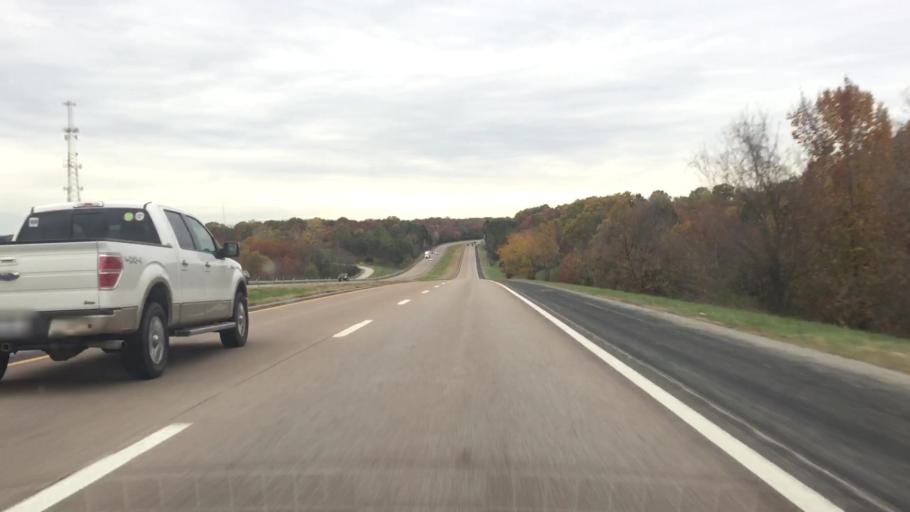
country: US
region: Missouri
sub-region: Boone County
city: Ashland
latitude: 38.6747
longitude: -92.2423
